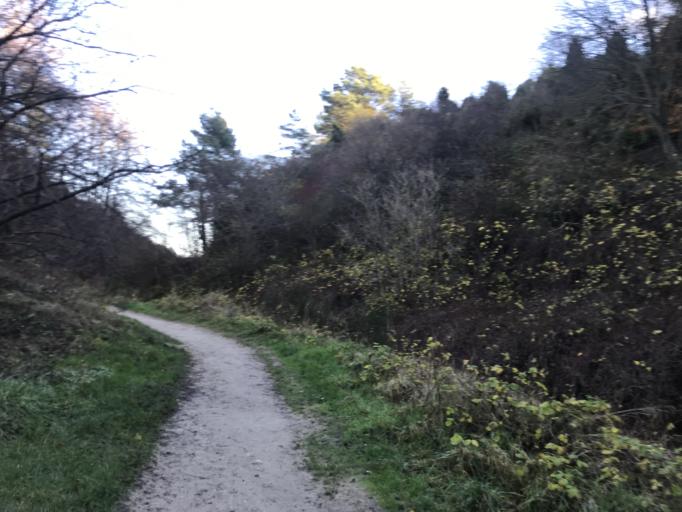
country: PL
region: Pomeranian Voivodeship
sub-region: Powiat pucki
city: Chlapowo
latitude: 54.8114
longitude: 18.3684
